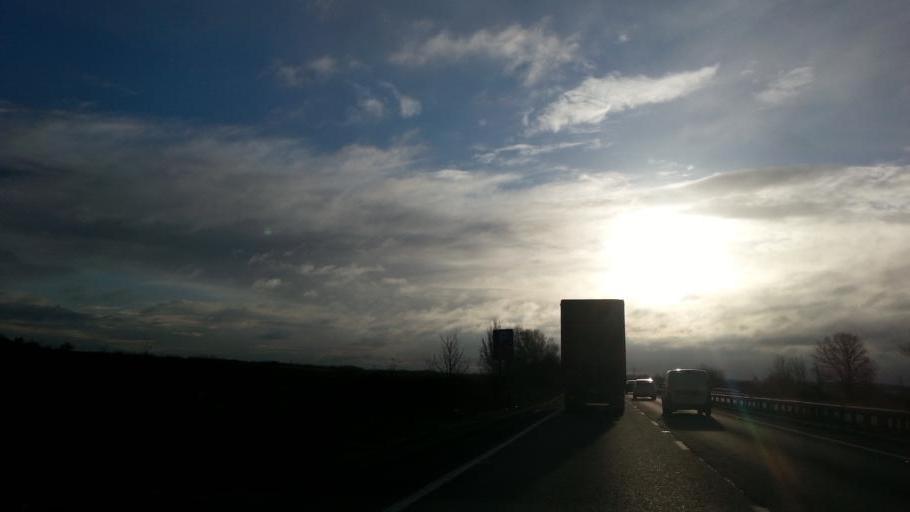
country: GB
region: England
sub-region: Cambridgeshire
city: Great Stukeley
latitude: 52.3541
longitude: -0.2280
